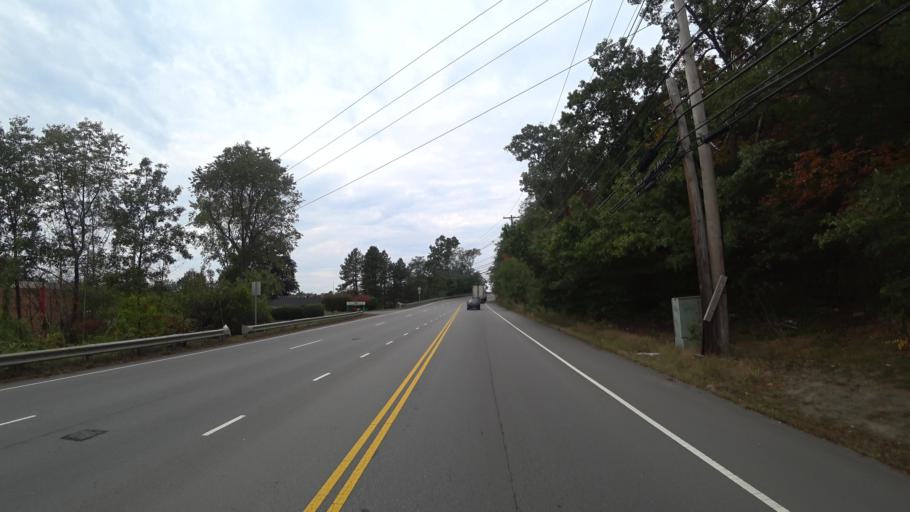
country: US
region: Massachusetts
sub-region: Middlesex County
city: Wilmington
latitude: 42.5906
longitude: -71.1595
